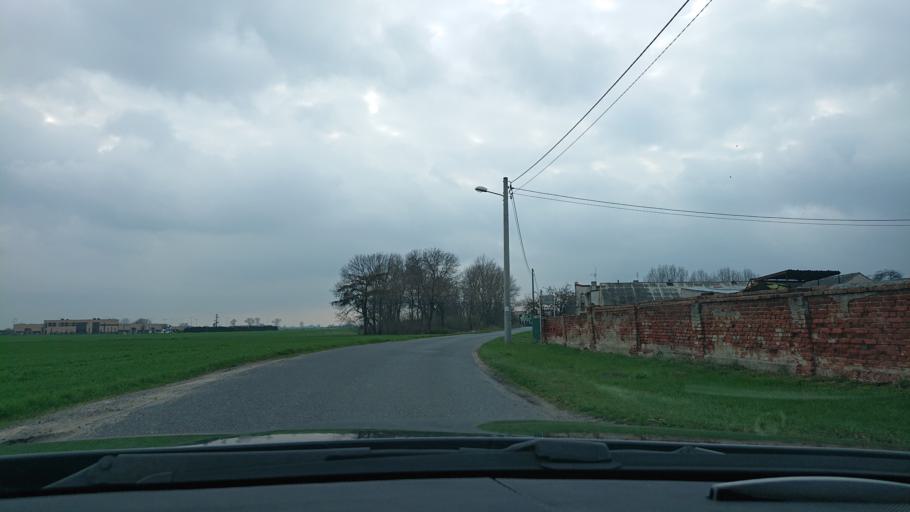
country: PL
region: Greater Poland Voivodeship
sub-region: Powiat gnieznienski
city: Lubowo
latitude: 52.5292
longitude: 17.4891
